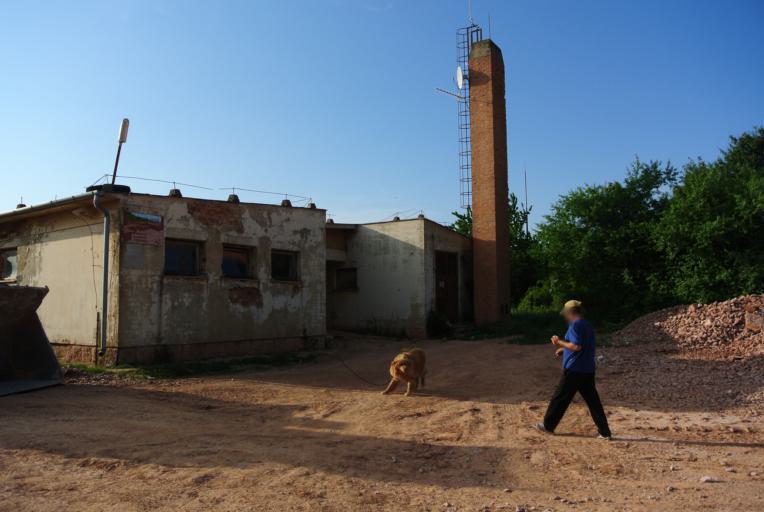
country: HU
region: Komarom-Esztergom
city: Tardos
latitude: 47.6582
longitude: 18.4743
